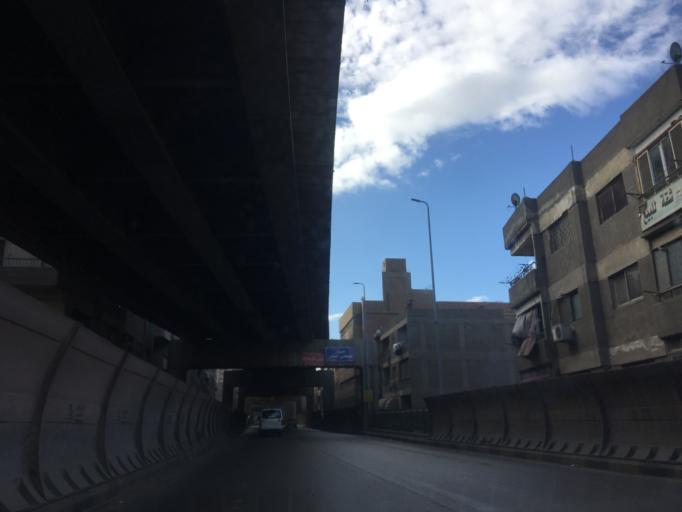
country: EG
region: Al Jizah
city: Al Jizah
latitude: 30.0305
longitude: 31.1824
